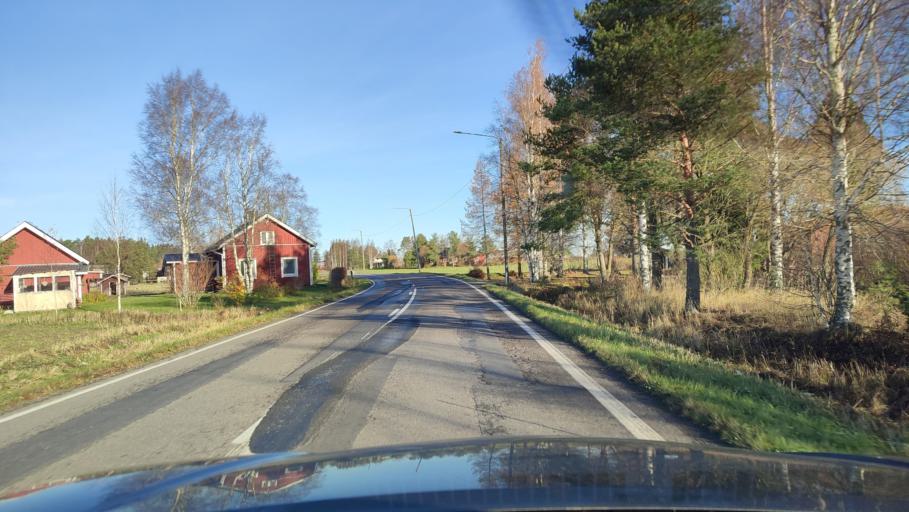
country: FI
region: Southern Ostrobothnia
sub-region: Suupohja
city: Teuva
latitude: 62.4557
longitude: 21.7115
